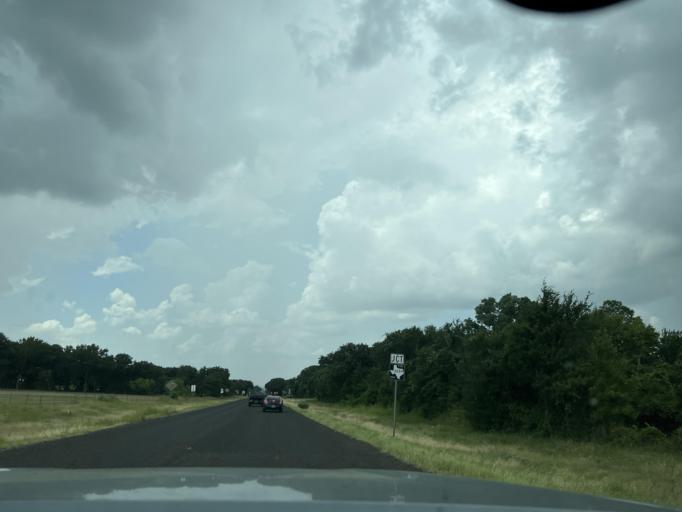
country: US
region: Texas
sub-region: Wise County
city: Decatur
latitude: 33.1609
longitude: -97.6297
